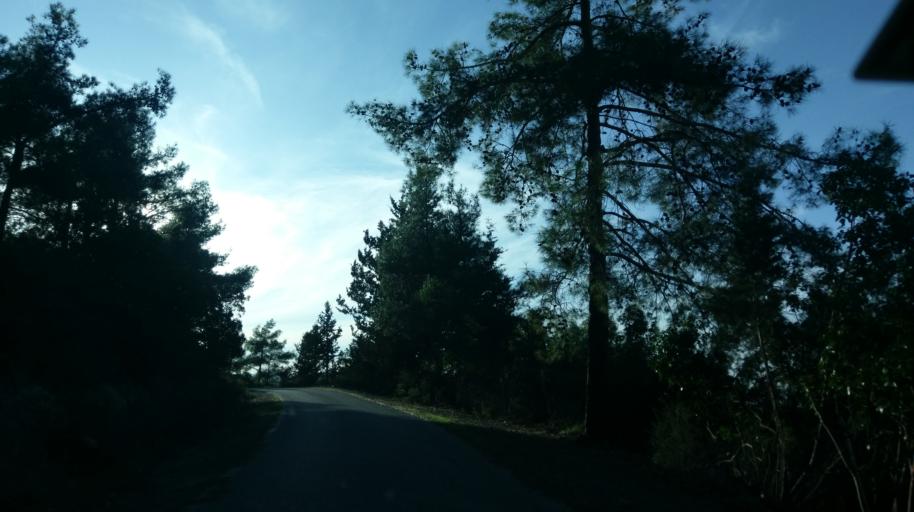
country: CY
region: Ammochostos
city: Lefkonoiko
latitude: 35.3184
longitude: 33.5870
